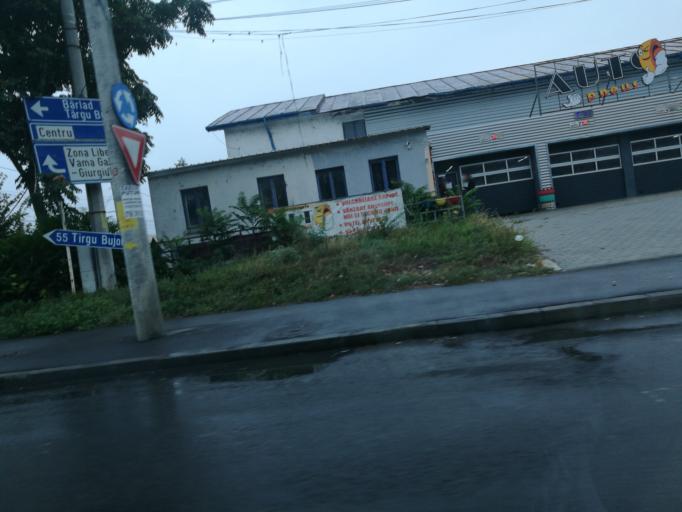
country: RO
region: Galati
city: Galati
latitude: 45.4652
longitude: 28.0354
